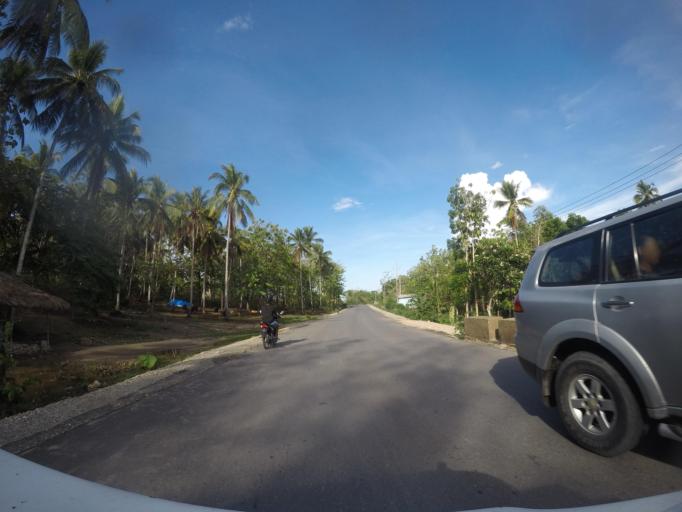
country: TL
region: Baucau
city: Baucau
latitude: -8.4966
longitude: 126.4533
